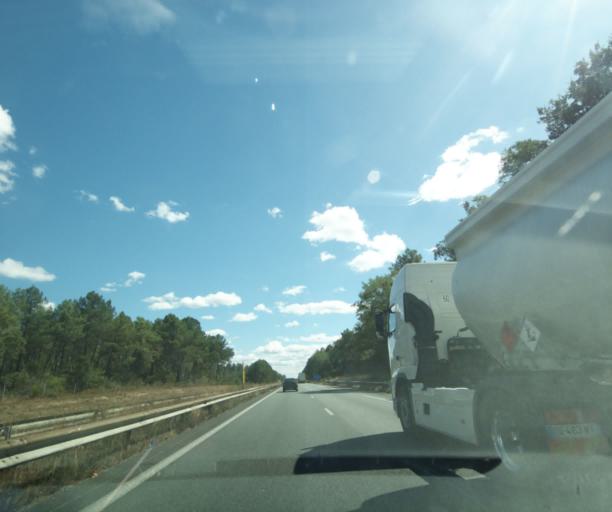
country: FR
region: Aquitaine
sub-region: Departement de la Gironde
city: Saint-Selve
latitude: 44.6677
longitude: -0.4677
